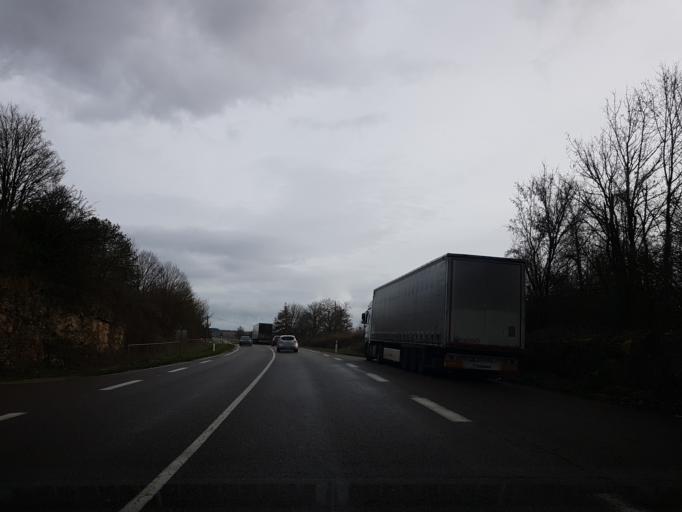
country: FR
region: Franche-Comte
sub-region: Departement de la Haute-Saone
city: Frotey-les-Vesoul
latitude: 47.6247
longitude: 6.1858
